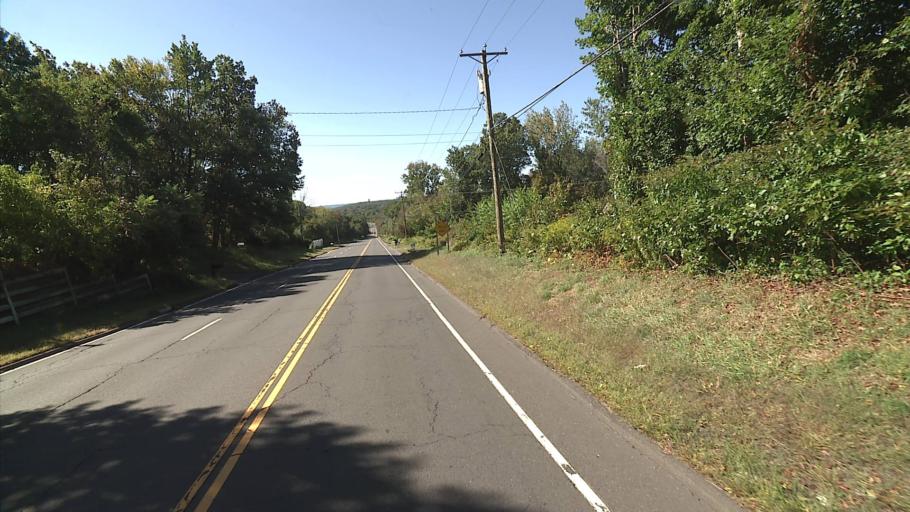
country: US
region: Connecticut
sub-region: New Haven County
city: Wolcott
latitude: 41.6142
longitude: -72.9797
